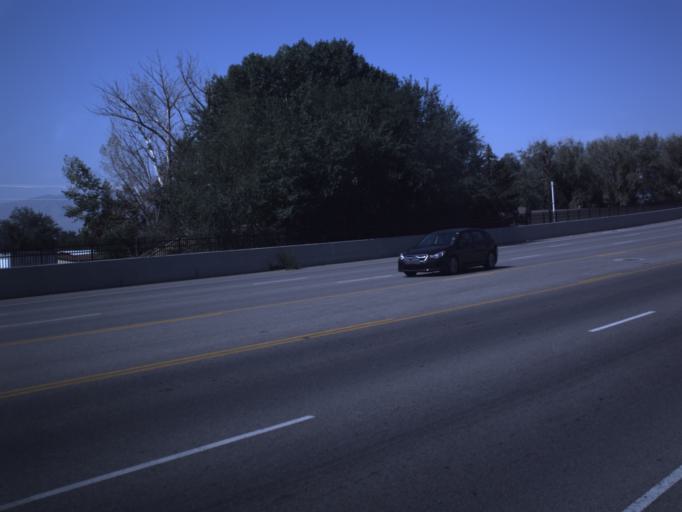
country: US
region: Utah
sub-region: Utah County
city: Pleasant Grove
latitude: 40.3594
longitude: -111.7418
